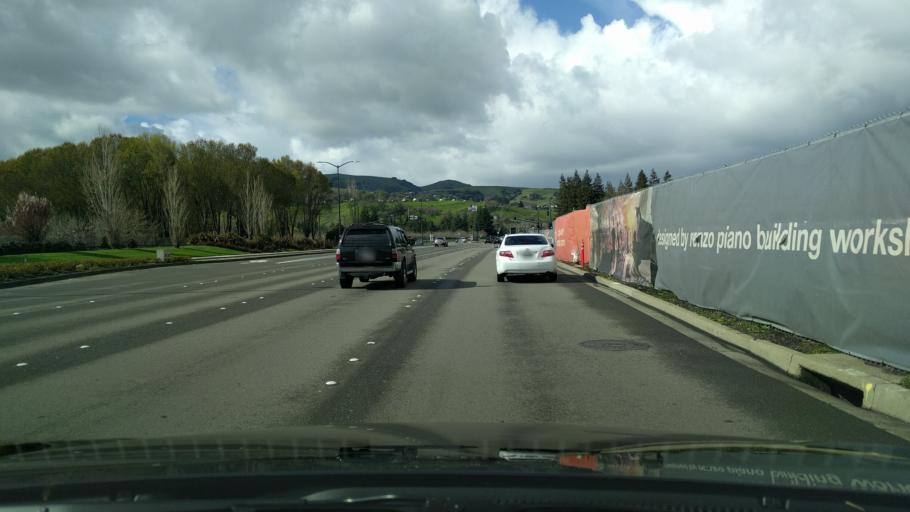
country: US
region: California
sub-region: Contra Costa County
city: San Ramon
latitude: 37.7622
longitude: -121.9584
